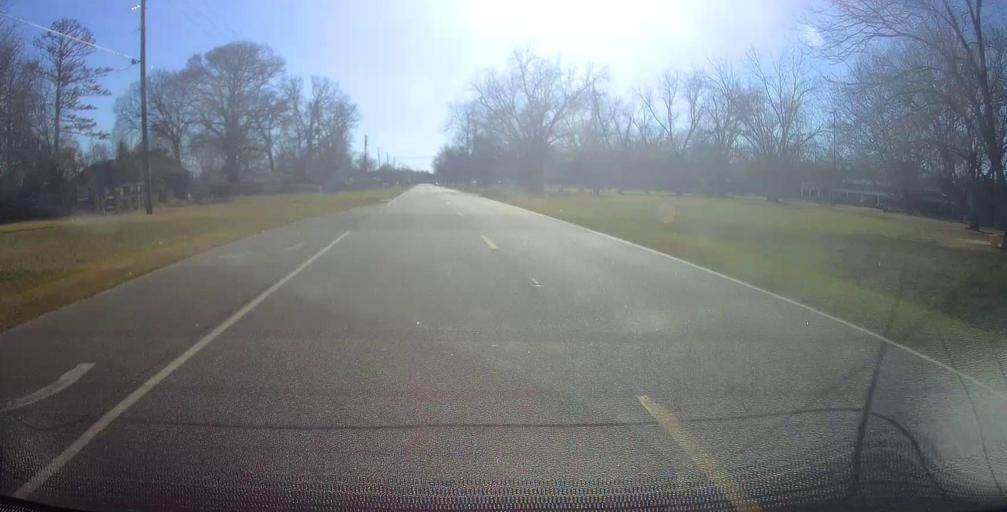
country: US
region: Georgia
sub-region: Sumter County
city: Americus
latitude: 32.1031
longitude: -84.2072
